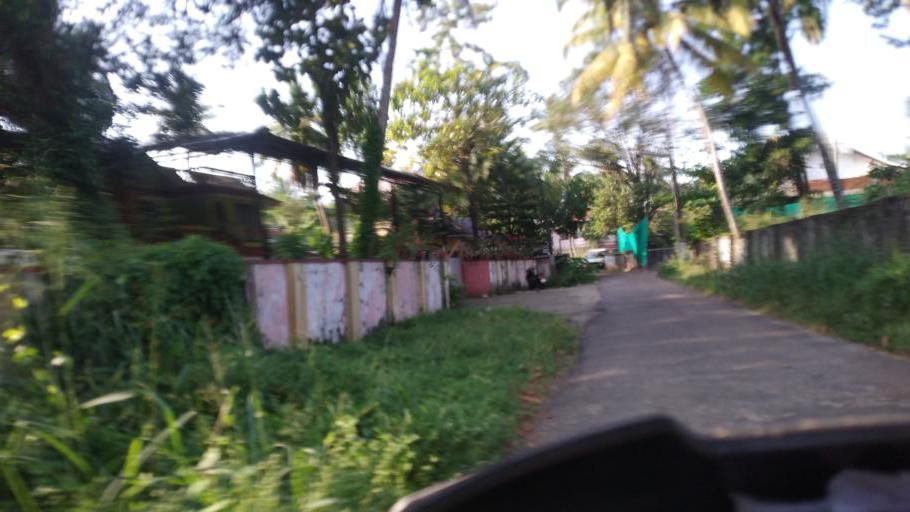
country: IN
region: Kerala
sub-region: Ernakulam
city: Elur
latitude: 10.0512
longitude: 76.2185
